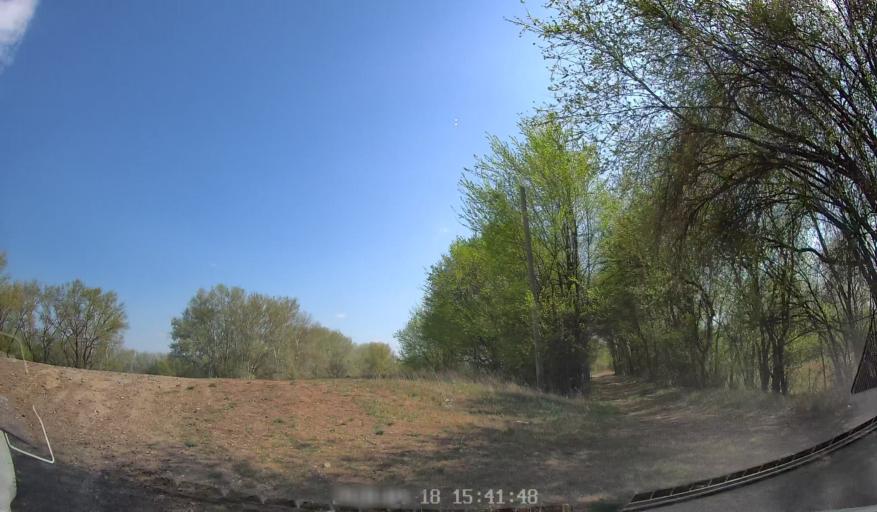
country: MD
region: Chisinau
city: Vadul lui Voda
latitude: 47.1429
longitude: 29.0962
